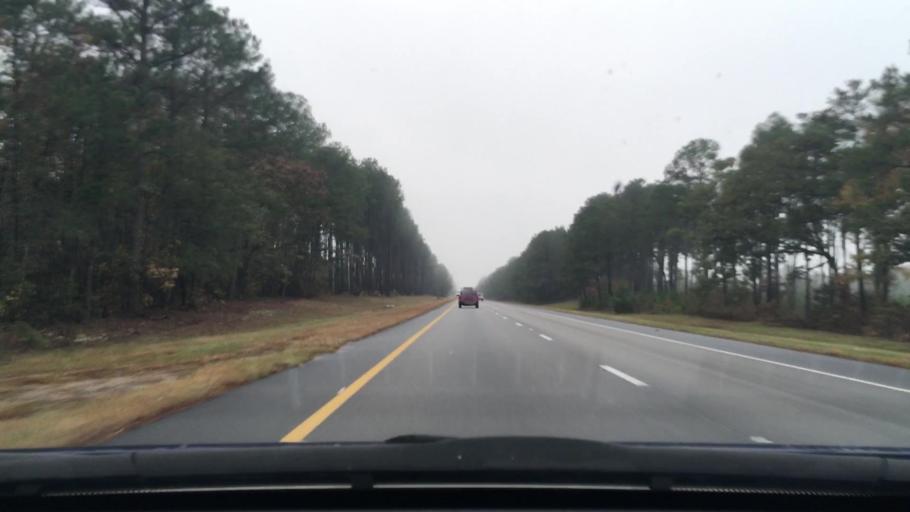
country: US
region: South Carolina
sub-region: Lee County
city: Bishopville
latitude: 34.2026
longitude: -80.3605
